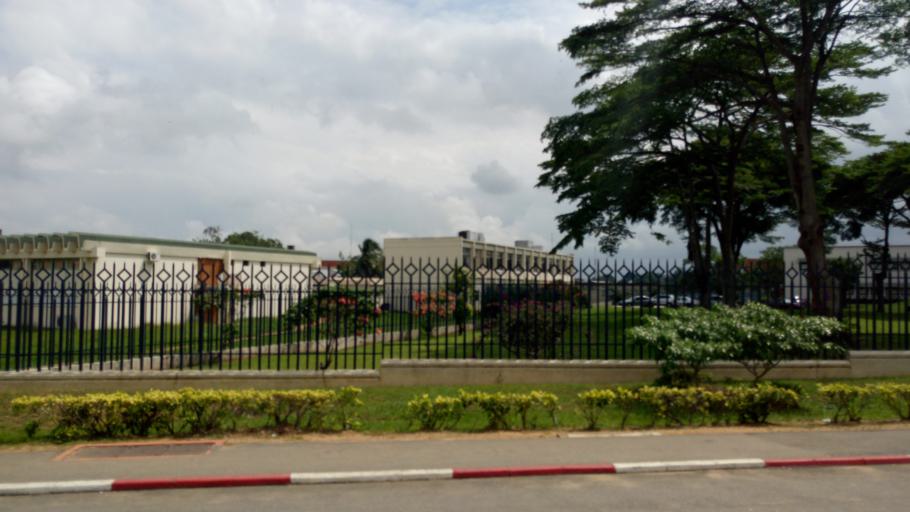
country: CI
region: Lagunes
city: Abidjan
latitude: 5.3488
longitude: -3.9881
